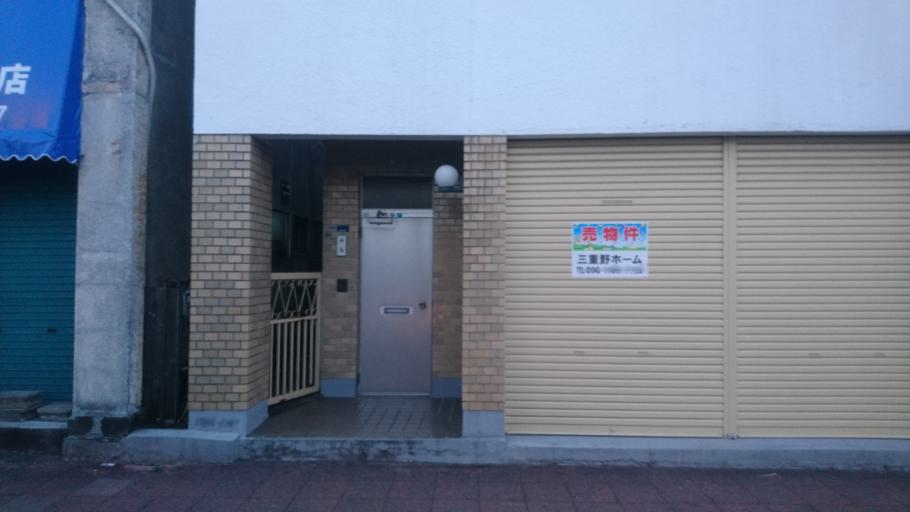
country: JP
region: Miyazaki
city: Miyazaki-shi
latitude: 31.8996
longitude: 131.4183
